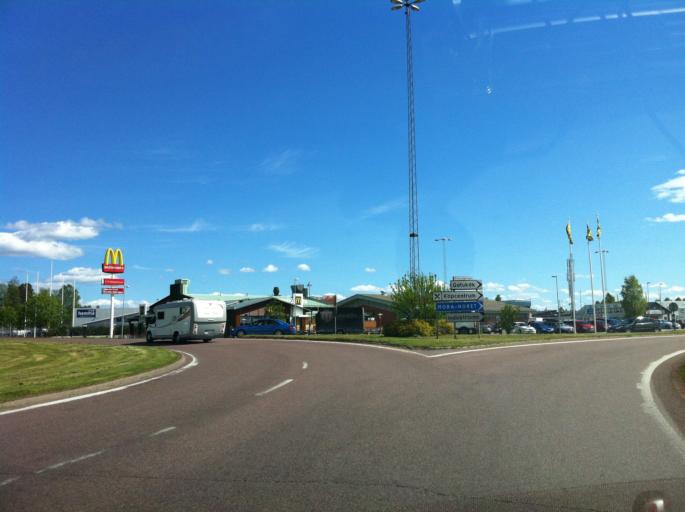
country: SE
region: Dalarna
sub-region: Mora Kommun
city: Mora
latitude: 61.0094
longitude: 14.5850
